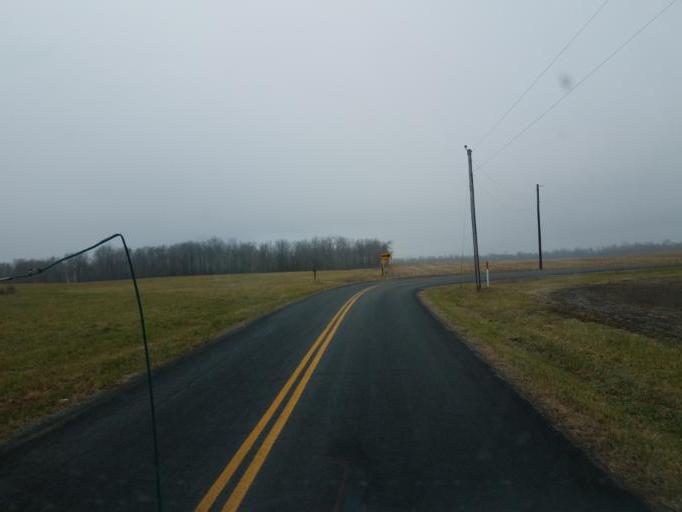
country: US
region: Ohio
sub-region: Champaign County
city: North Lewisburg
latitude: 40.2410
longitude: -83.5474
